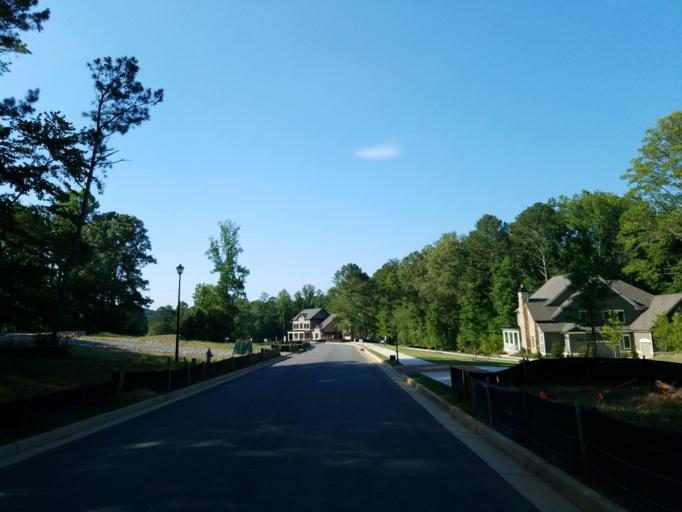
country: US
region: Georgia
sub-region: Fulton County
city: Milton
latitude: 34.1570
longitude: -84.3402
